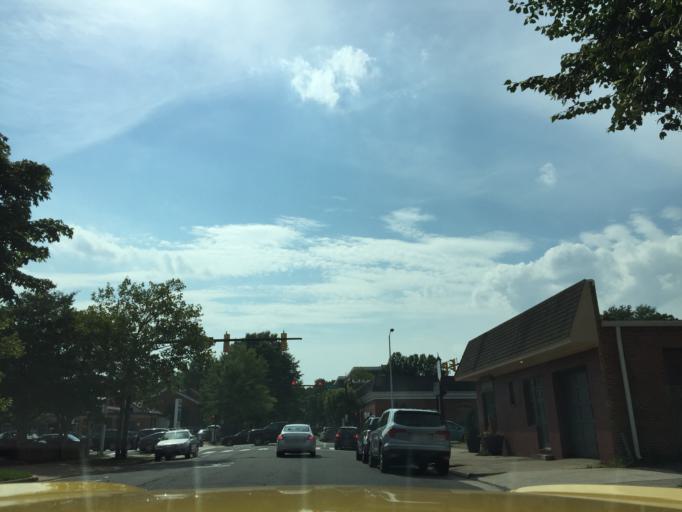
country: US
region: Virginia
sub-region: City of Alexandria
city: Alexandria
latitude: 38.8005
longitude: -77.0473
